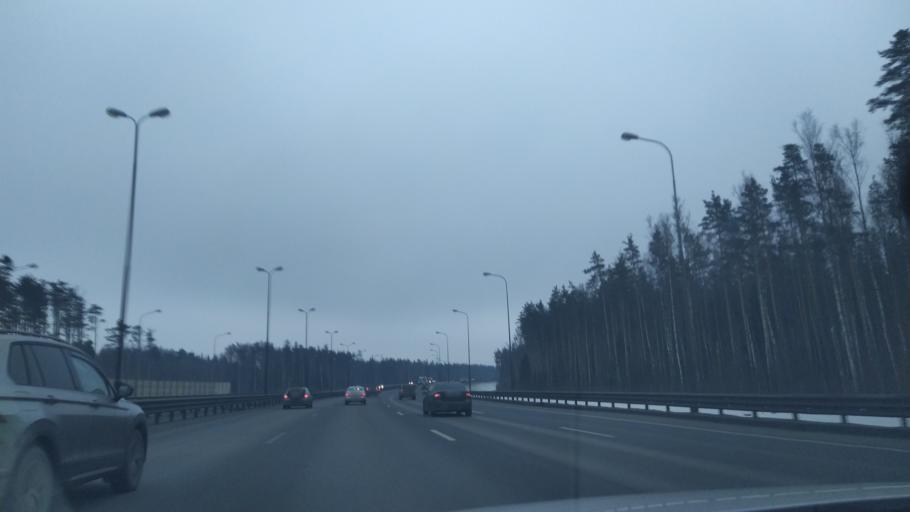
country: RU
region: St.-Petersburg
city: Krasnogvargeisky
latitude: 59.9702
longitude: 30.5497
